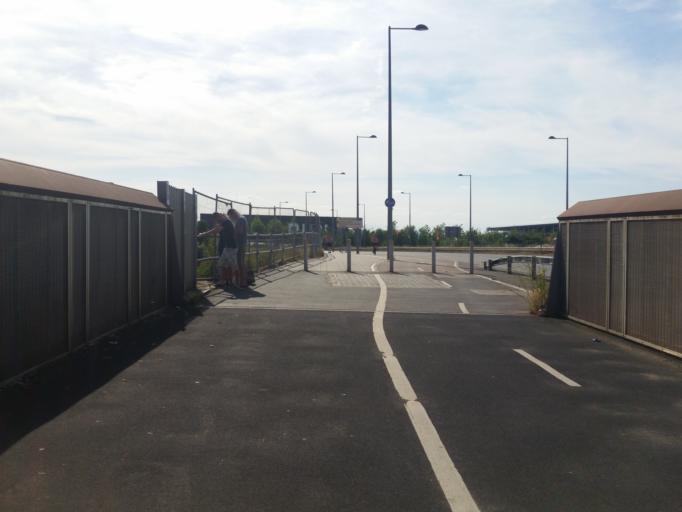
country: GB
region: England
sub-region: Greater London
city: Poplar
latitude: 51.5441
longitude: -0.0136
